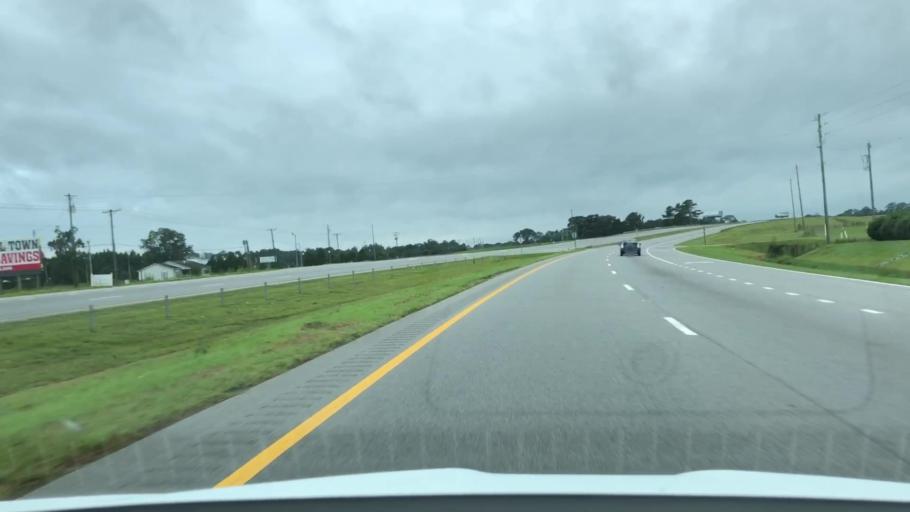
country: US
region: North Carolina
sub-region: Lenoir County
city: Kinston
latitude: 35.2606
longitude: -77.6619
